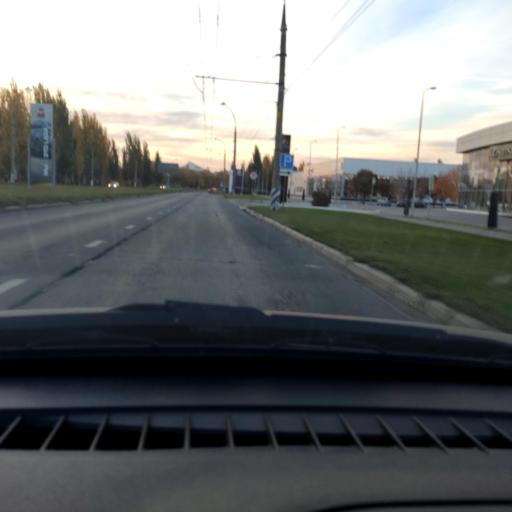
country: RU
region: Samara
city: Tol'yatti
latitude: 53.5455
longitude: 49.2758
